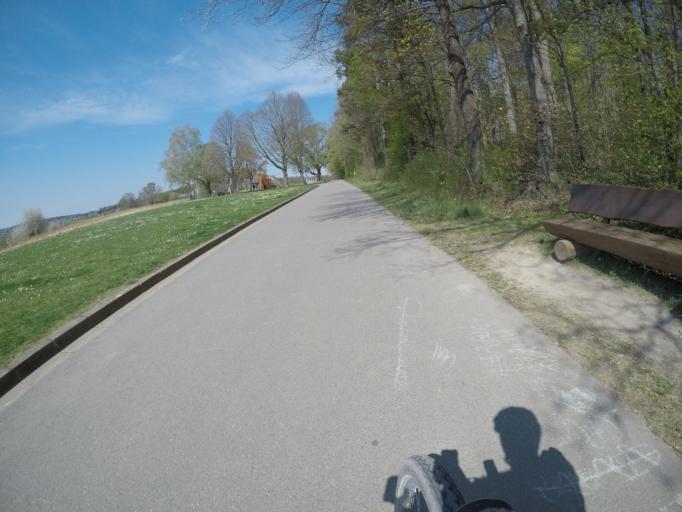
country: DE
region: Baden-Wuerttemberg
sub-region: Regierungsbezirk Stuttgart
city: Rutesheim
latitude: 48.8198
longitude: 8.9714
